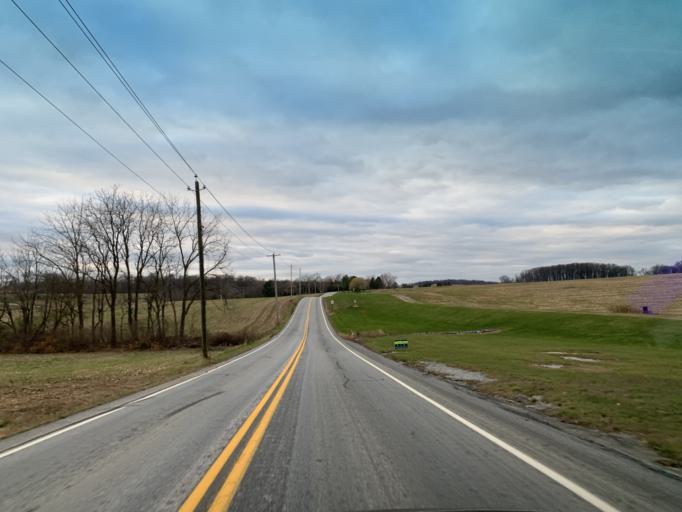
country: US
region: Pennsylvania
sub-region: York County
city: Stewartstown
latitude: 39.7746
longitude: -76.6010
